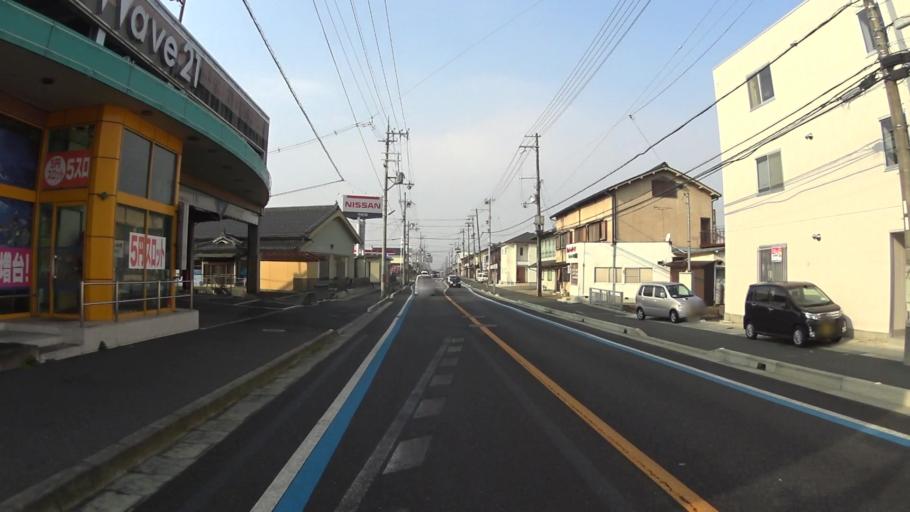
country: JP
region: Kyoto
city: Fukuchiyama
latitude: 35.2976
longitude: 135.1614
